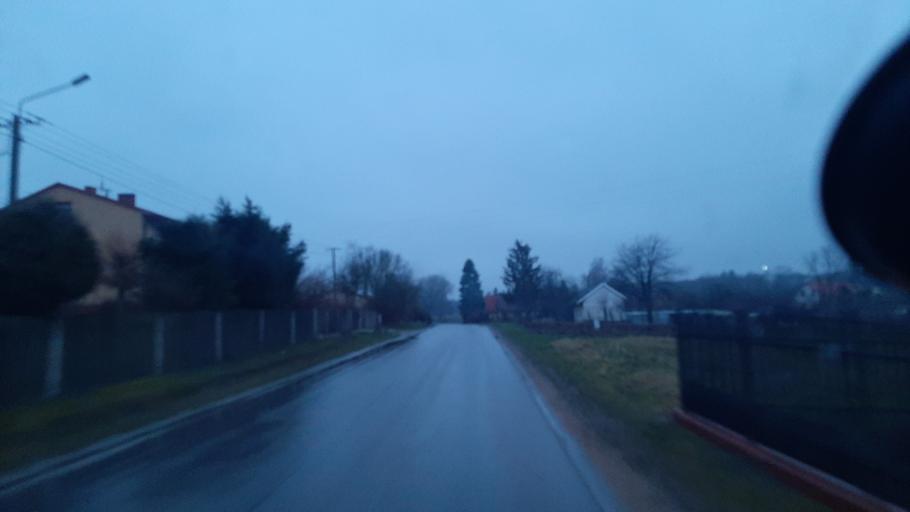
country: PL
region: Lublin Voivodeship
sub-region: Powiat lubartowski
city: Kamionka
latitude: 51.4031
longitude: 22.4139
